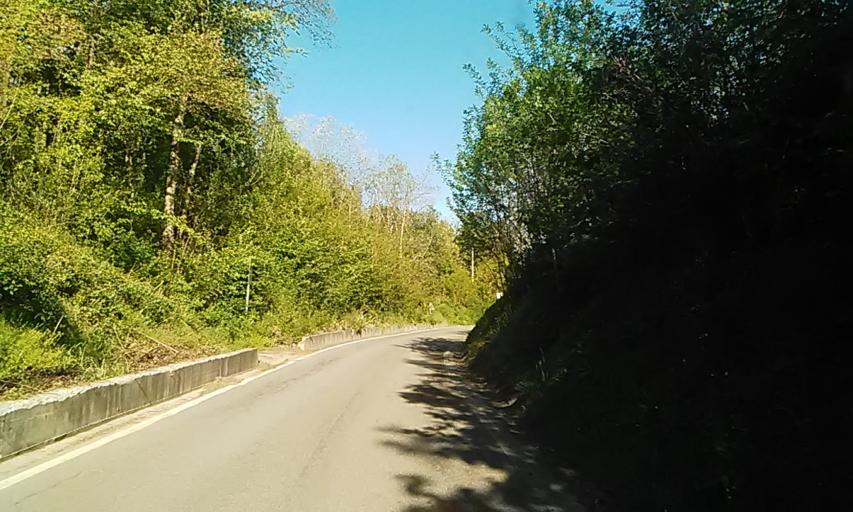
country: IT
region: Piedmont
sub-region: Provincia di Novara
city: Cavaglio D'Agogna
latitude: 45.6118
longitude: 8.4754
